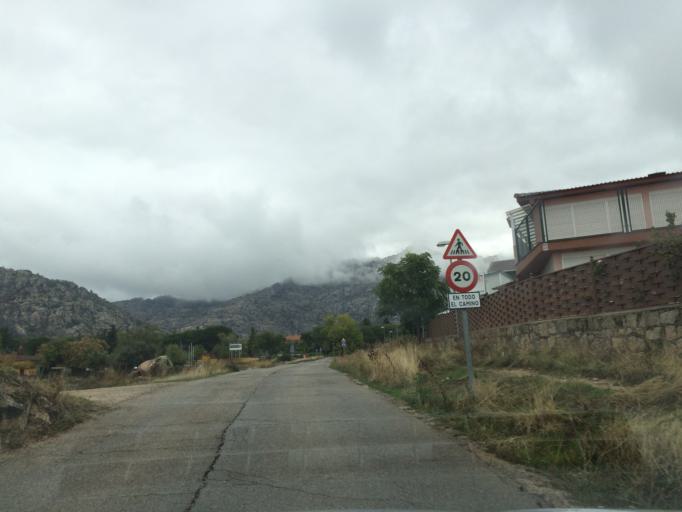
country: ES
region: Madrid
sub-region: Provincia de Madrid
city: Manzanares el Real
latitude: 40.7247
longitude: -3.8763
